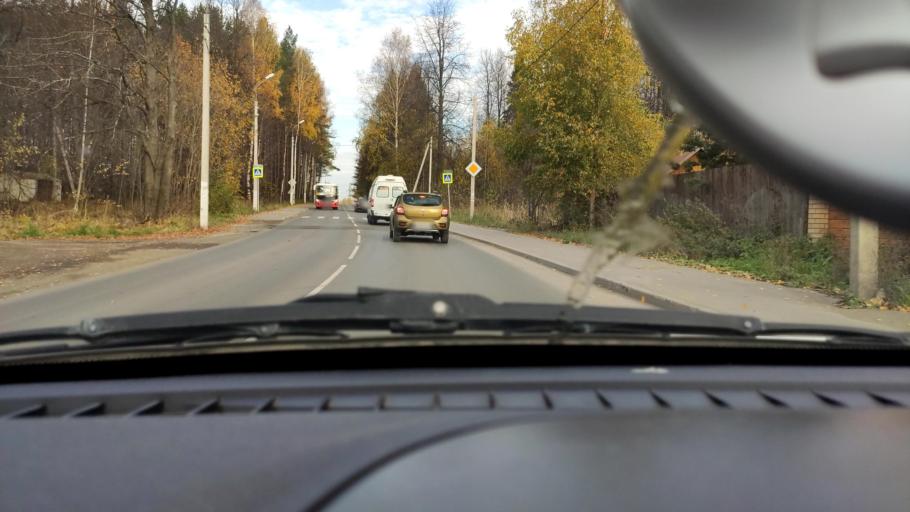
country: RU
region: Perm
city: Perm
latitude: 58.0920
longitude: 56.4041
